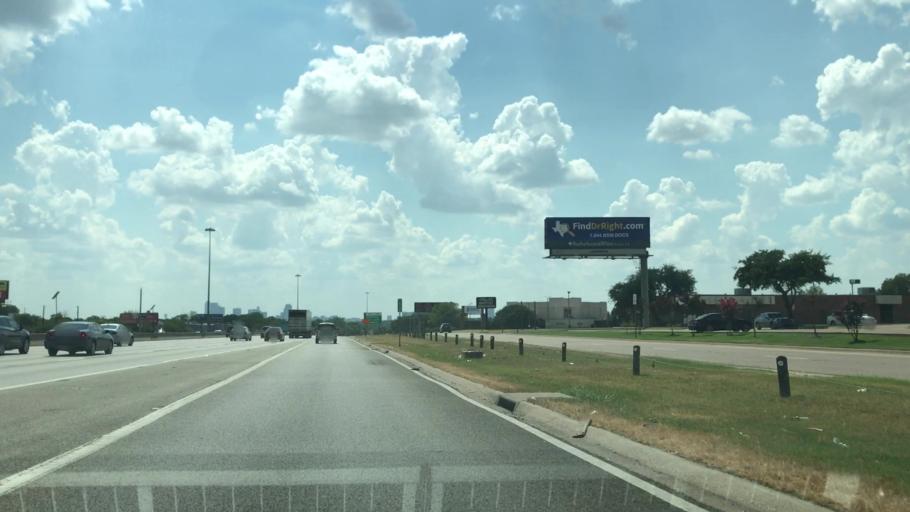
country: US
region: Texas
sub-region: Dallas County
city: Highland Park
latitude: 32.7942
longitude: -96.7032
